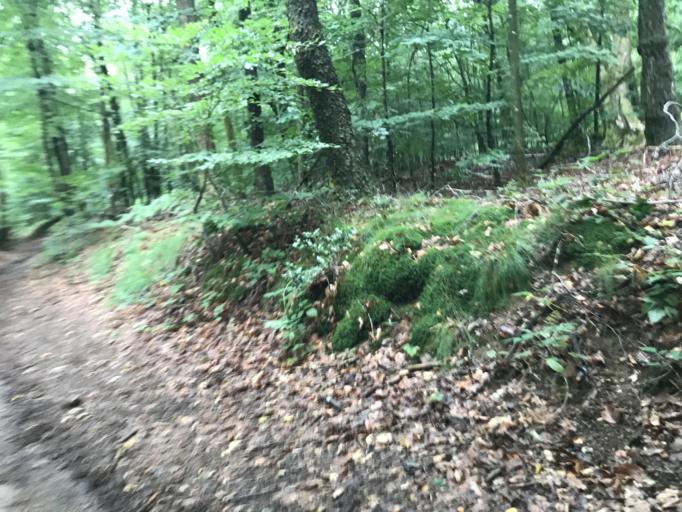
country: FR
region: Champagne-Ardenne
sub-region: Departement des Ardennes
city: Thilay
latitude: 49.8936
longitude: 4.7757
